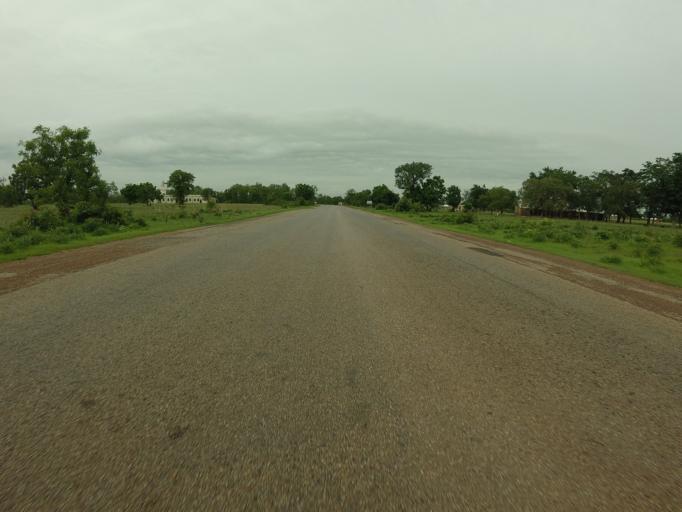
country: GH
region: Northern
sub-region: Yendi
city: Yendi
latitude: 9.5079
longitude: -0.0276
